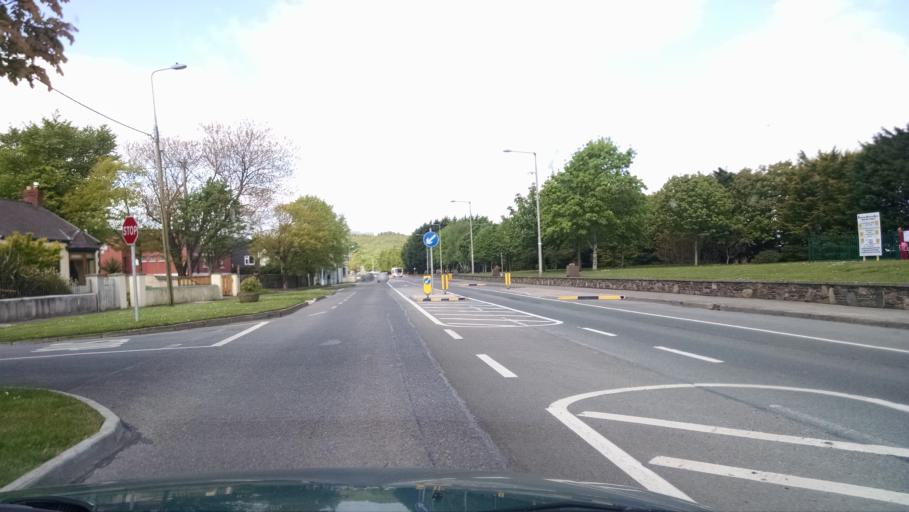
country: IE
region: Munster
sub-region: County Cork
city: Cobh
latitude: 51.8303
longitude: -8.3195
